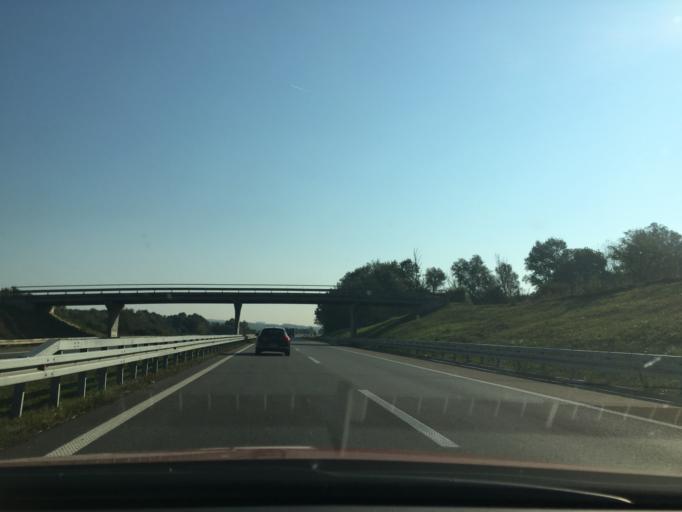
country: RS
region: Central Serbia
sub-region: Podunavski Okrug
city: Smederevo
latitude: 44.5852
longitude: 20.8479
